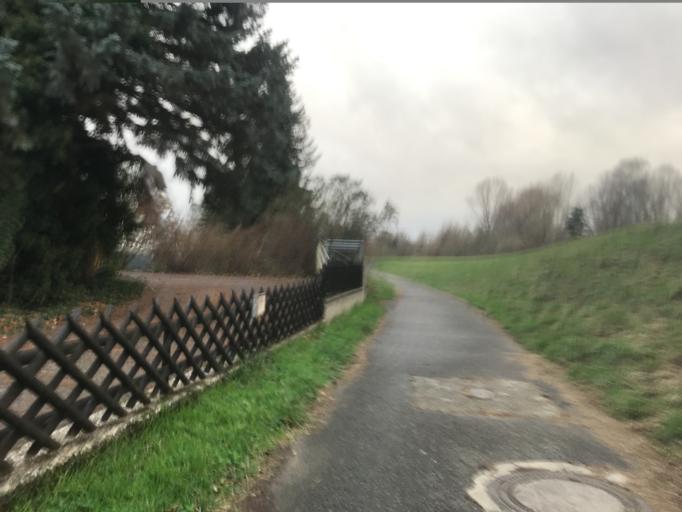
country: DE
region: Rheinland-Pfalz
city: Oestrich-Winkel
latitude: 49.9908
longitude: 8.0175
